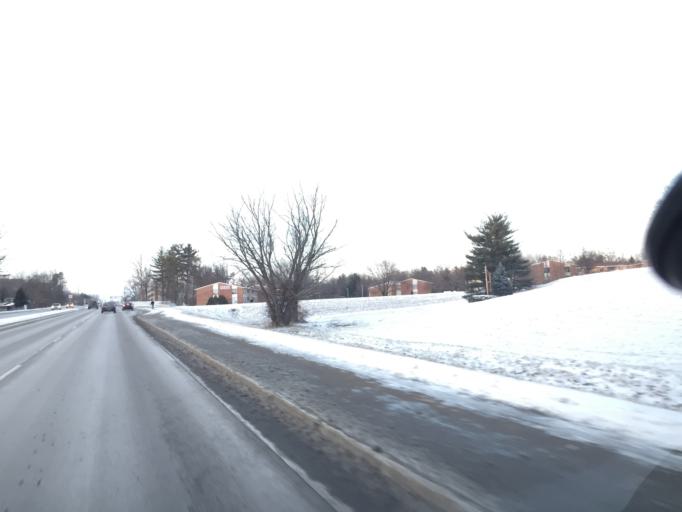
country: US
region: Indiana
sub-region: Monroe County
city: Bloomington
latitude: 39.1664
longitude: -86.4994
